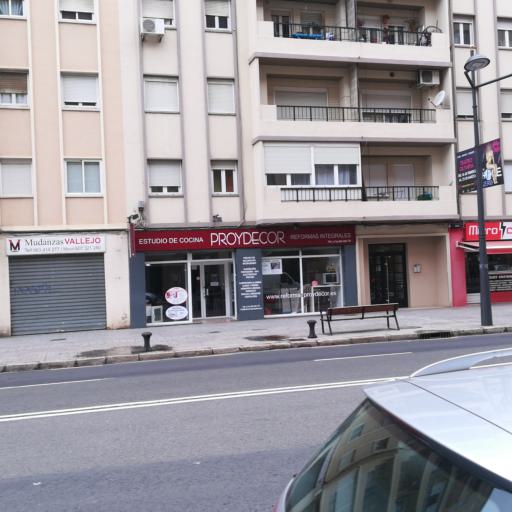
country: ES
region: Valencia
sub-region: Provincia de Valencia
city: Valencia
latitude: 39.4555
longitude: -0.3842
